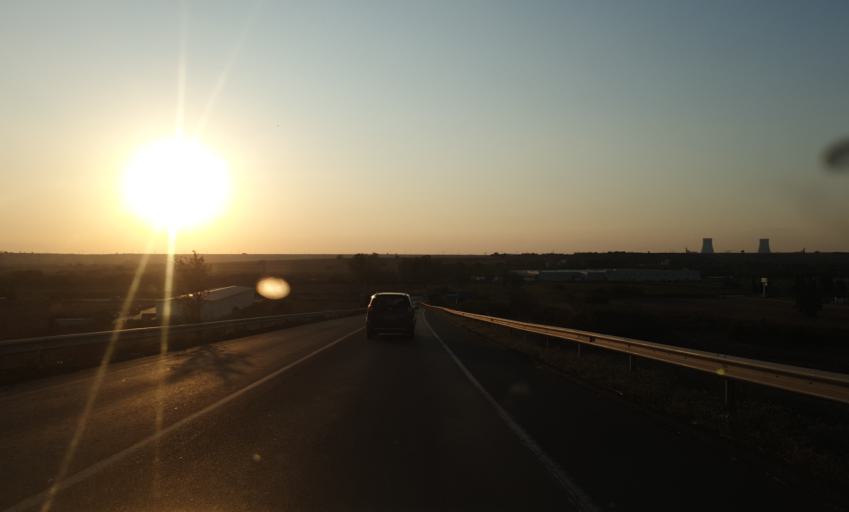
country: TR
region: Kirklareli
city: Luleburgaz
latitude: 41.4418
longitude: 27.3836
